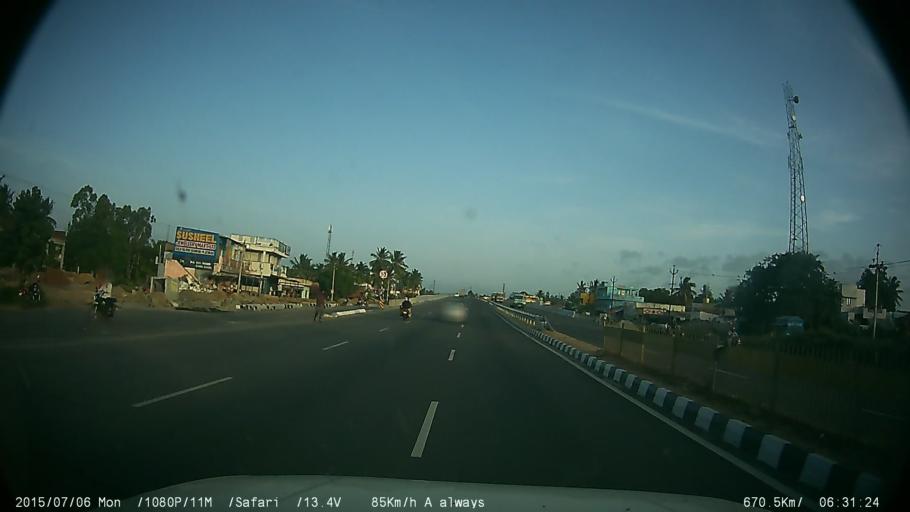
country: IN
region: Tamil Nadu
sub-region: Krishnagiri
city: Kelamangalam
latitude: 12.6828
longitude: 77.9401
